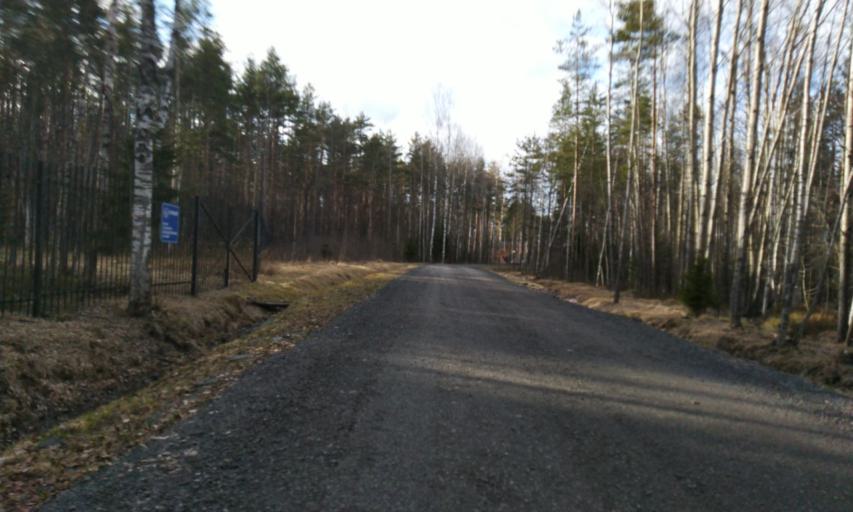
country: RU
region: Leningrad
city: Toksovo
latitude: 60.1214
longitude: 30.4764
